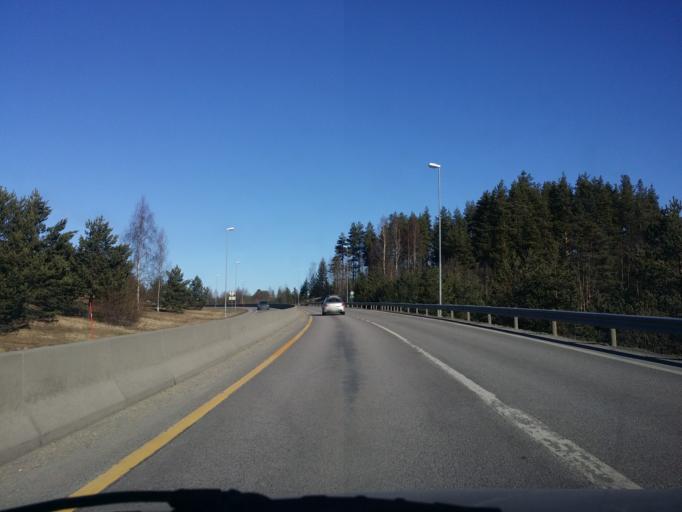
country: NO
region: Buskerud
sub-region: Ringerike
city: Honefoss
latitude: 60.2021
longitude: 10.2600
